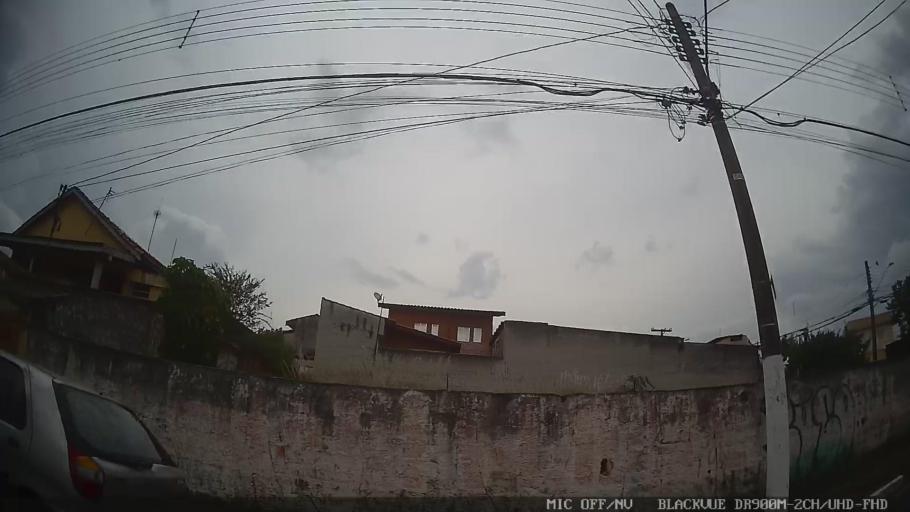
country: BR
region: Sao Paulo
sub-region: Atibaia
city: Atibaia
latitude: -23.1192
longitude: -46.5598
